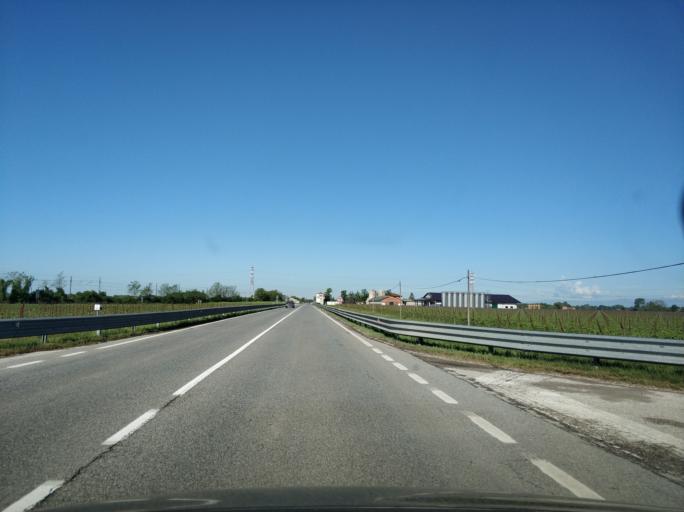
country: IT
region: Friuli Venezia Giulia
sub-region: Provincia di Udine
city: Torviscosa
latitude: 45.8284
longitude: 13.2542
